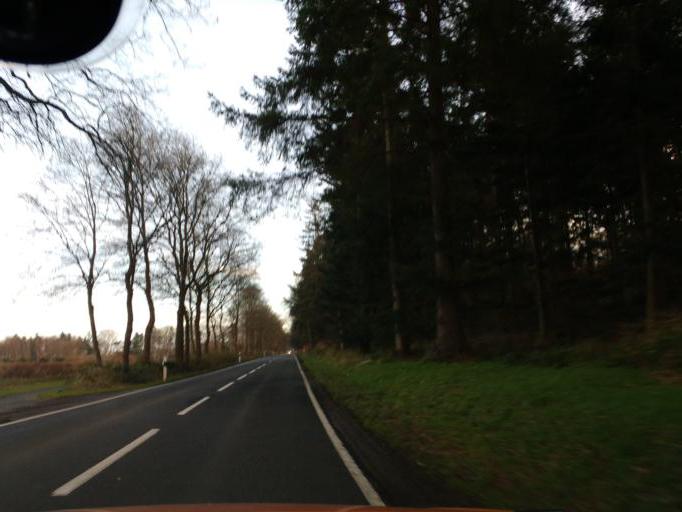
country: DE
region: Lower Saxony
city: Hude
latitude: 53.1175
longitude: 8.4067
